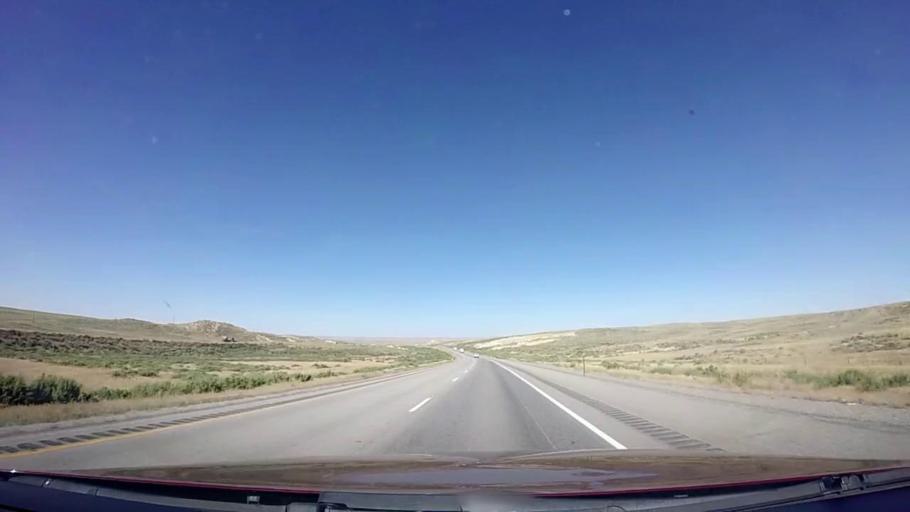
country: US
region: Wyoming
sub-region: Carbon County
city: Rawlins
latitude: 41.7893
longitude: -107.3857
